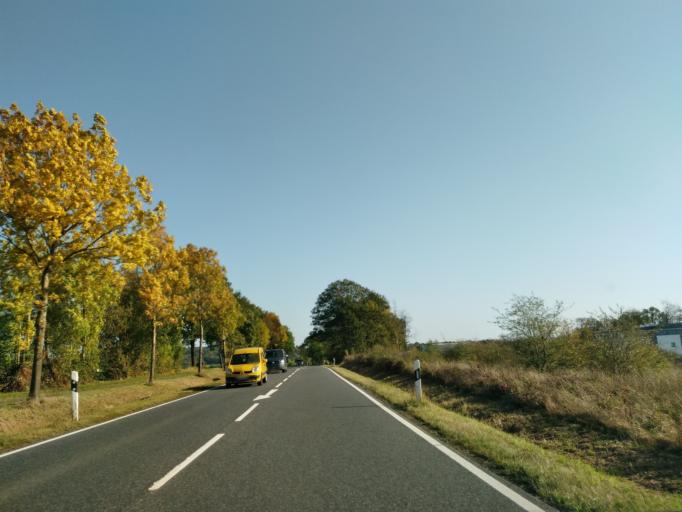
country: DE
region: Rheinland-Pfalz
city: Asbach
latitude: 50.7156
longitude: 7.4103
